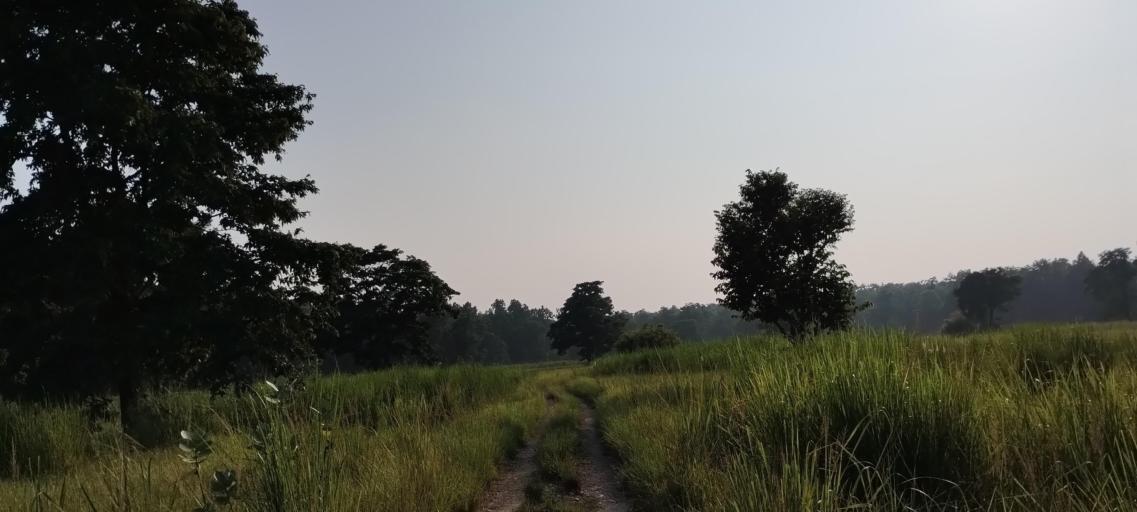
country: NP
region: Far Western
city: Tikapur
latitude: 28.5048
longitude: 81.2784
